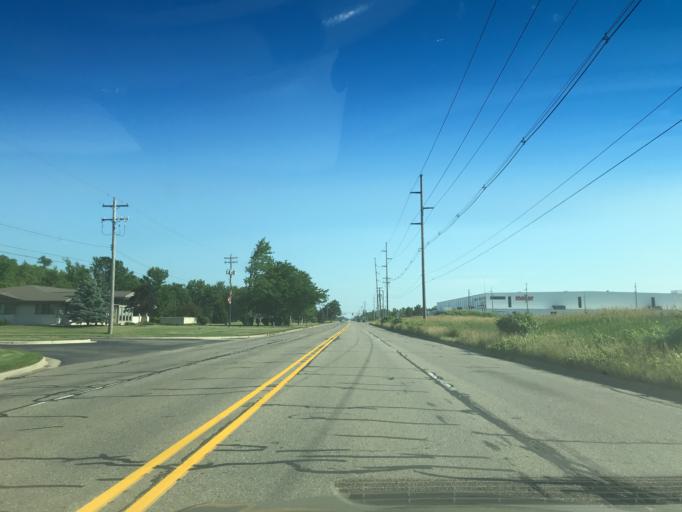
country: US
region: Michigan
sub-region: Eaton County
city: Waverly
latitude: 42.7158
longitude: -84.6424
